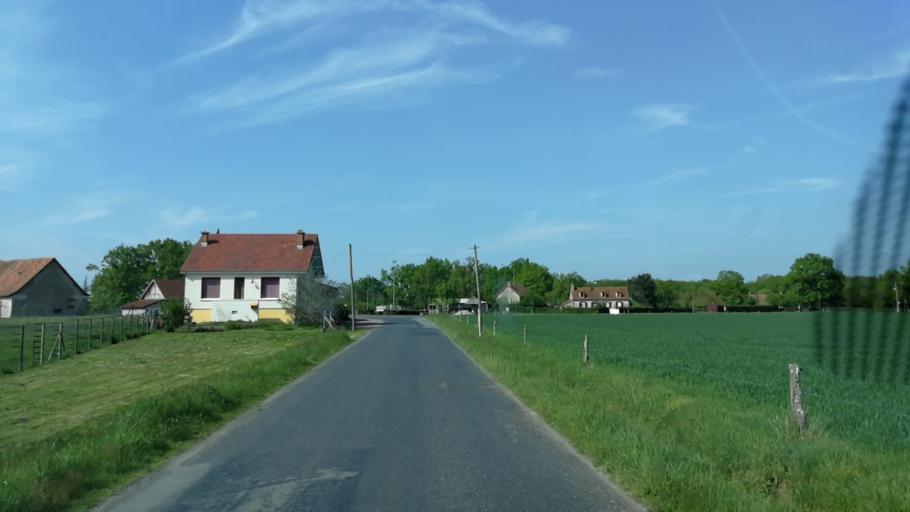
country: FR
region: Auvergne
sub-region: Departement de l'Allier
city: Neuilly-le-Real
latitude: 46.4064
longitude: 3.5758
